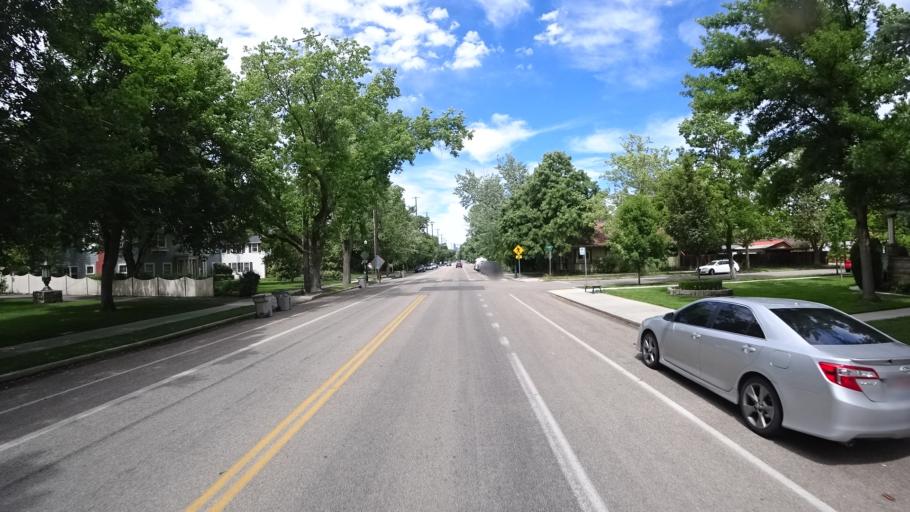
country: US
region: Idaho
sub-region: Ada County
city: Boise
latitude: 43.6080
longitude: -116.1848
